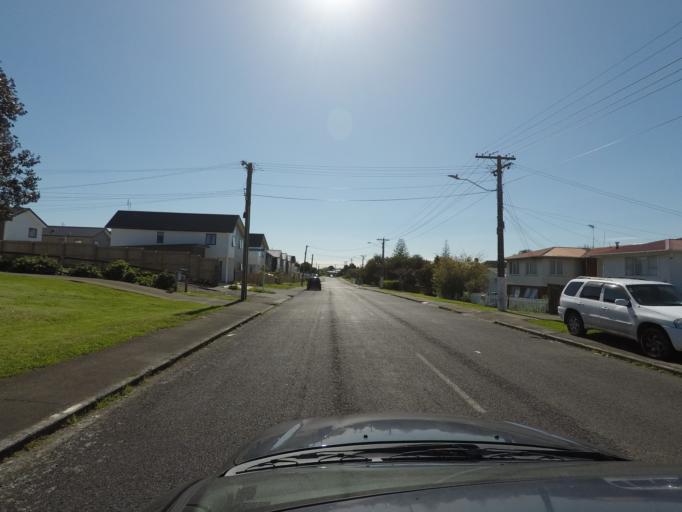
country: NZ
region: Auckland
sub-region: Auckland
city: Tamaki
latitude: -36.9272
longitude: 174.8602
